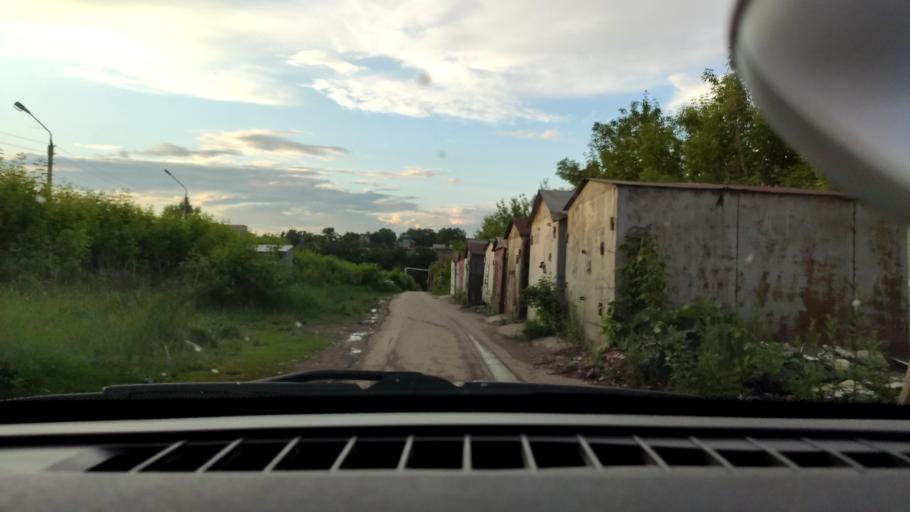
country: RU
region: Samara
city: Samara
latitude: 53.2498
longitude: 50.1817
